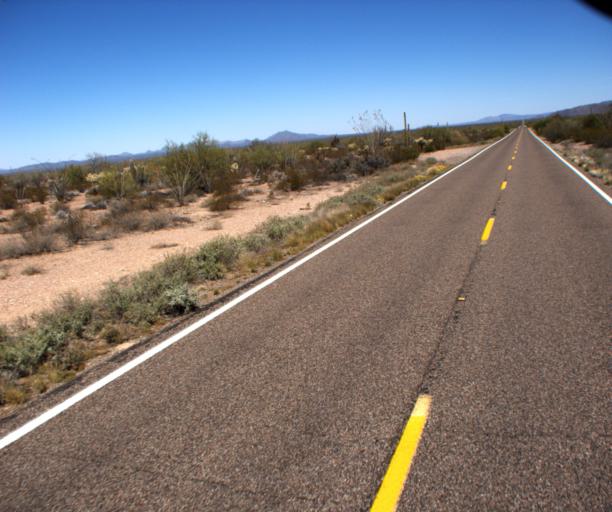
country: MX
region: Sonora
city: Sonoyta
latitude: 32.1049
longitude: -112.7706
